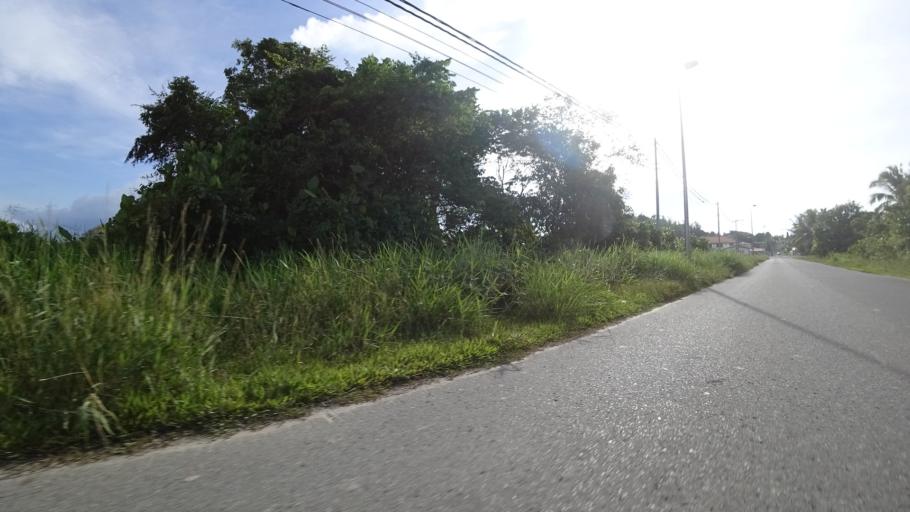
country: BN
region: Brunei and Muara
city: Bandar Seri Begawan
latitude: 4.8431
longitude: 114.8457
